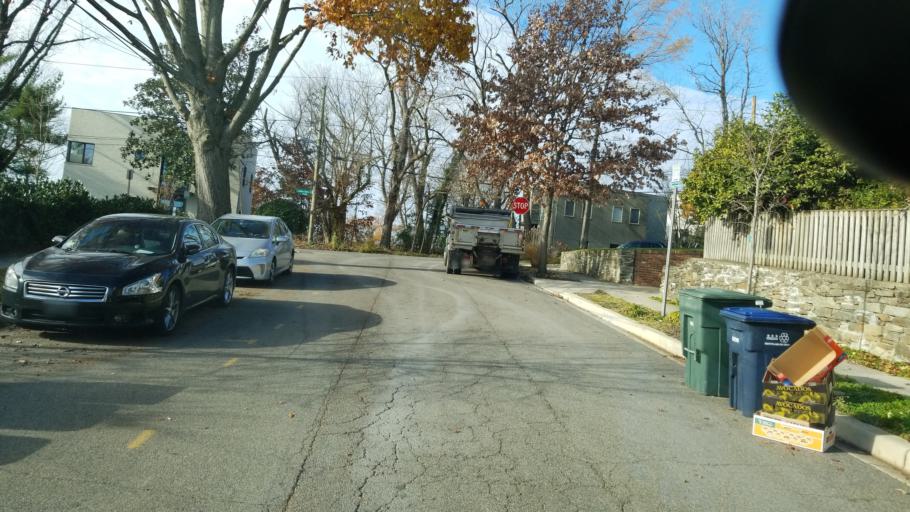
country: US
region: Virginia
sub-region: Arlington County
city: Arlington
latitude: 38.9115
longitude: -77.0877
